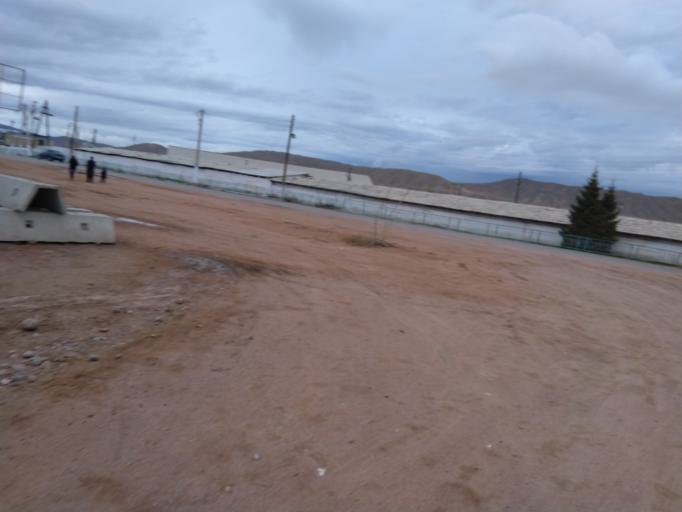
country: KG
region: Ysyk-Koel
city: Bokombayevskoye
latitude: 42.1153
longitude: 76.9838
